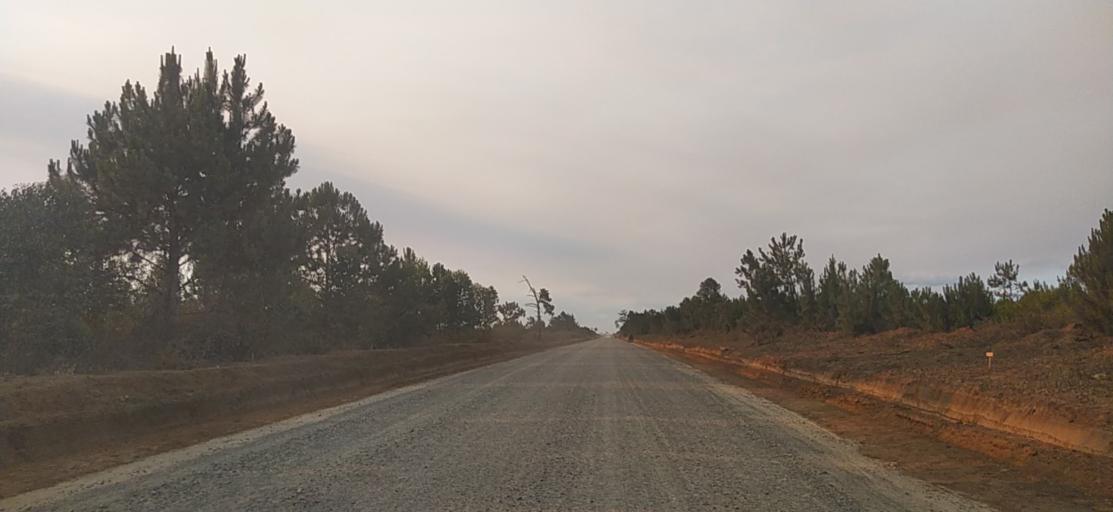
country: MG
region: Alaotra Mangoro
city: Moramanga
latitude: -18.5433
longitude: 48.2598
